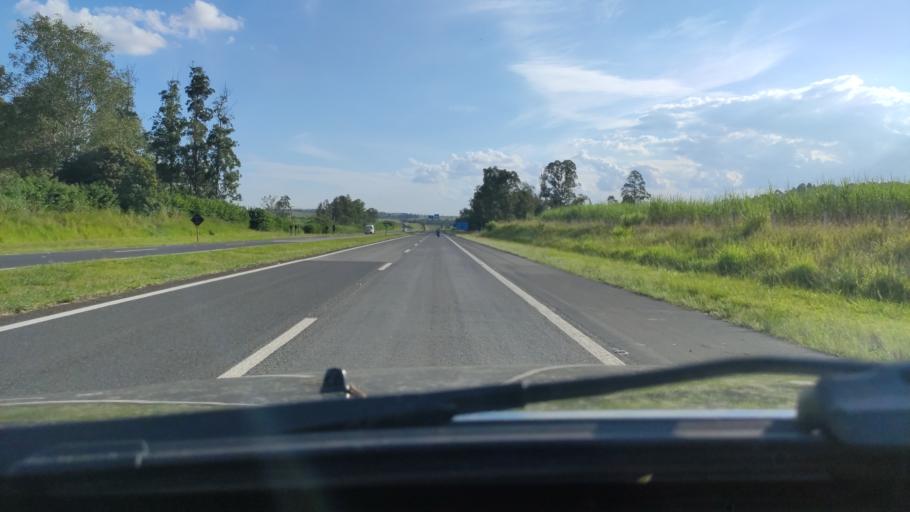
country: BR
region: Sao Paulo
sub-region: Mogi-Mirim
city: Mogi Mirim
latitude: -22.4512
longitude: -46.8904
